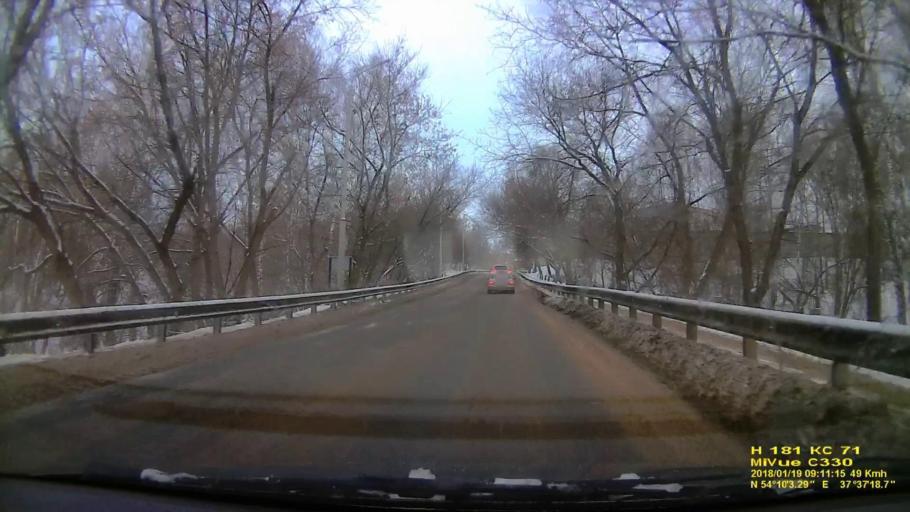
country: RU
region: Tula
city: Tula
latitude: 54.1657
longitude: 37.6213
